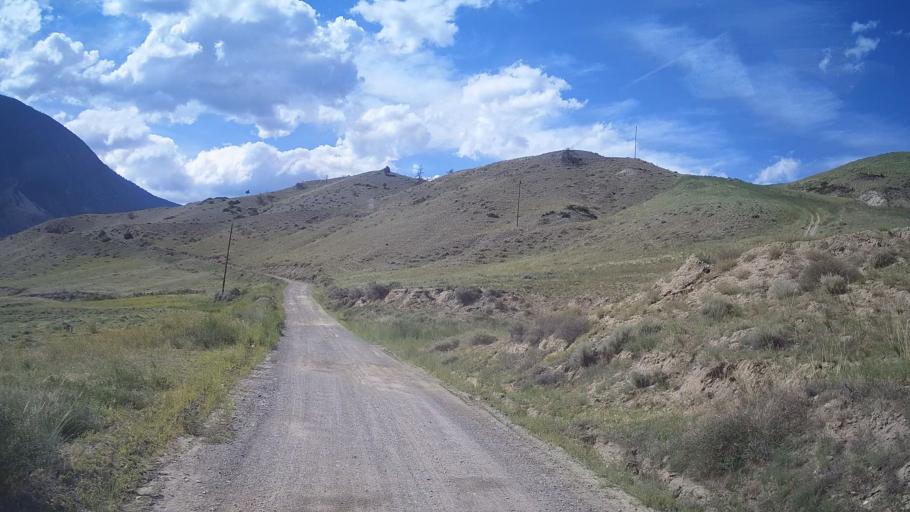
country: CA
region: British Columbia
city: Lillooet
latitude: 51.1815
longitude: -122.1141
